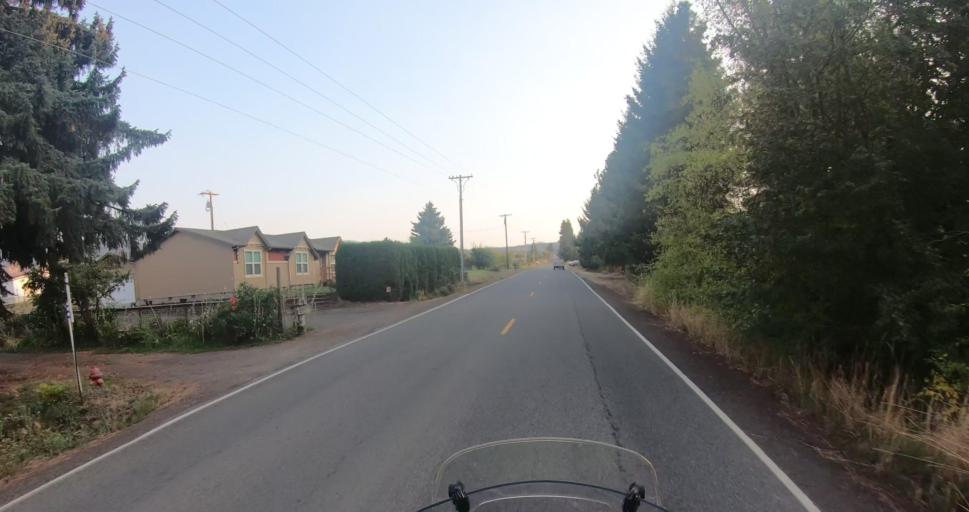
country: US
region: Oregon
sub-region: Hood River County
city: Odell
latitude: 45.5135
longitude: -121.5969
